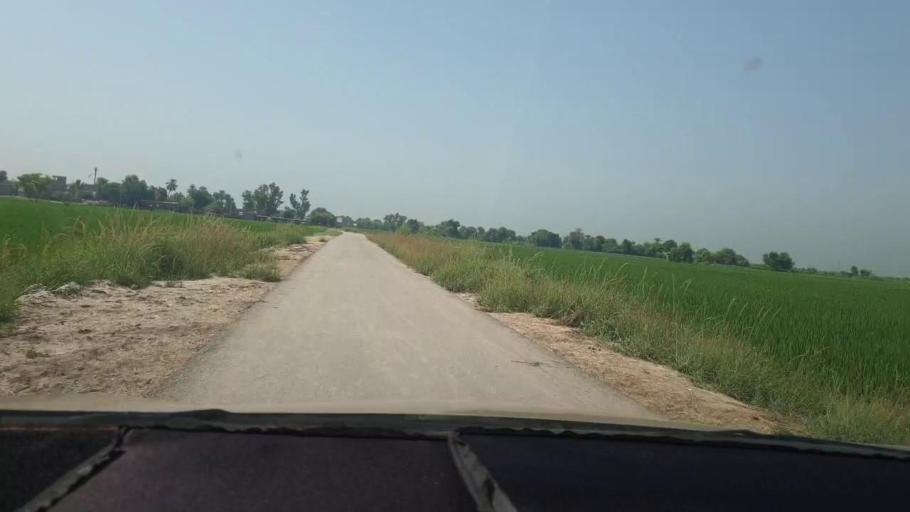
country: PK
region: Sindh
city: Kambar
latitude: 27.5583
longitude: 68.0421
